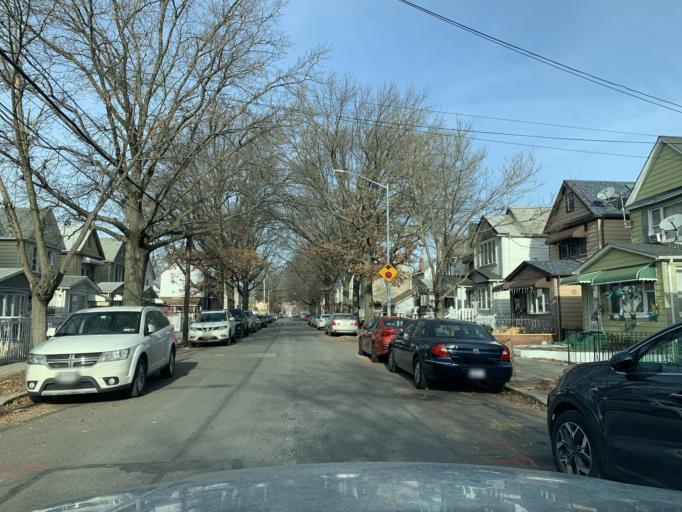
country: US
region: New York
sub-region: Queens County
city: Jamaica
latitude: 40.6872
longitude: -73.7775
